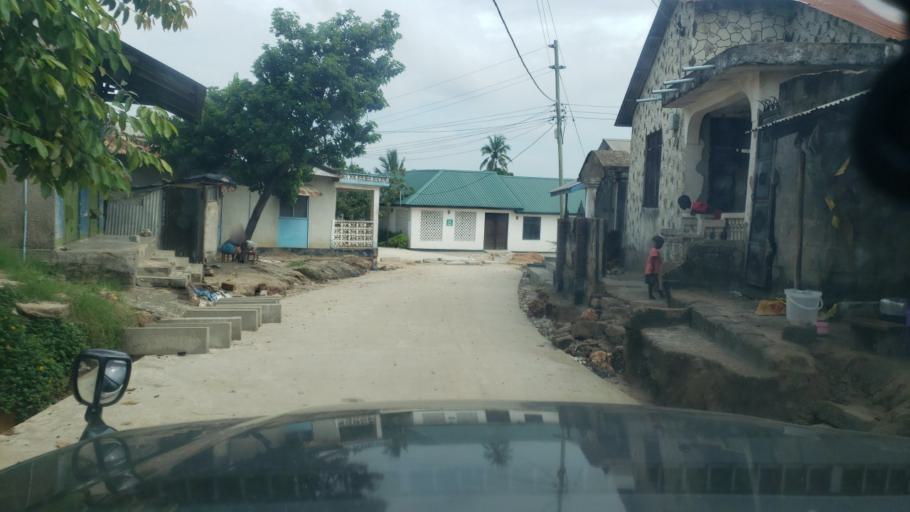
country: TZ
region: Pwani
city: Vikindu
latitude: -6.9238
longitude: 39.2553
